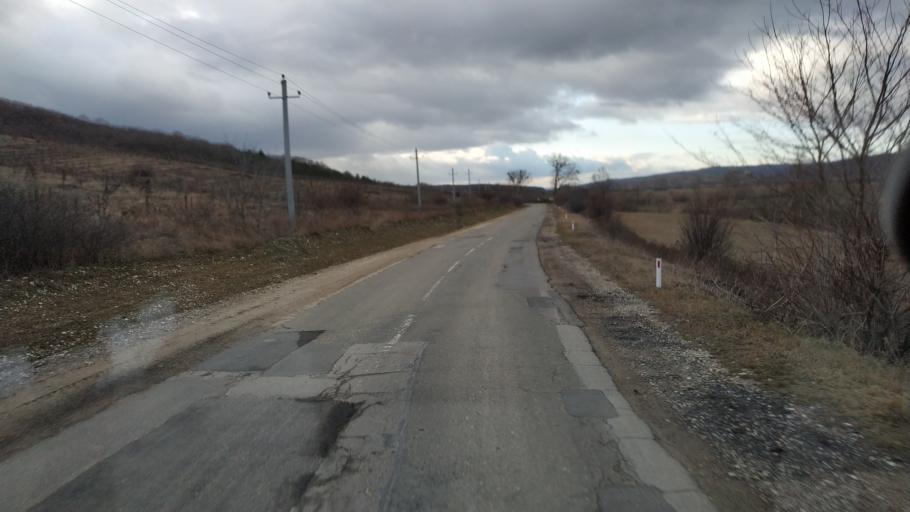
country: MD
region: Calarasi
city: Calarasi
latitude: 47.3124
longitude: 28.3432
